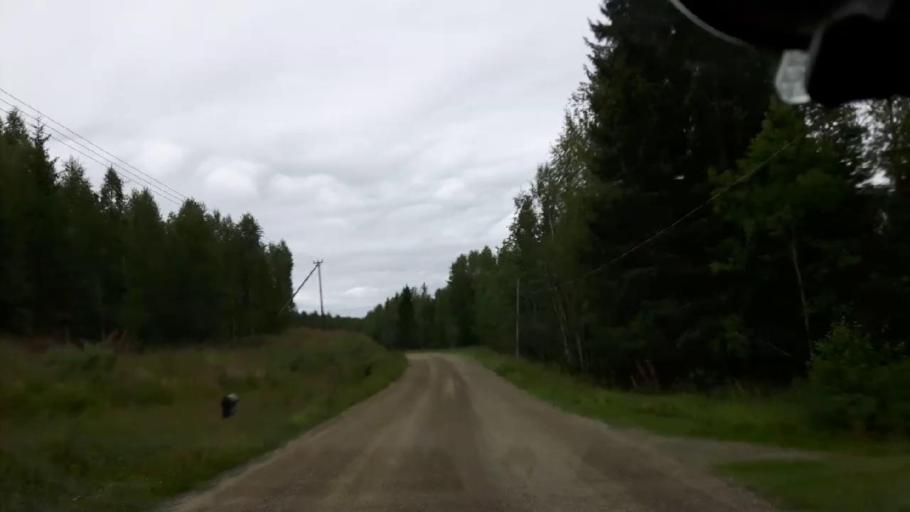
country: SE
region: Jaemtland
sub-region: Braecke Kommun
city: Braecke
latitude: 63.0213
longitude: 15.3737
